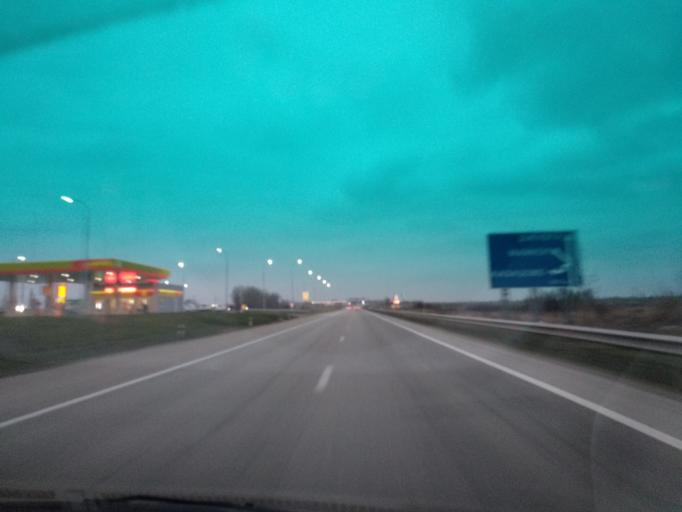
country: RU
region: Adygeya
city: Adygeysk
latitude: 44.9008
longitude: 39.1605
